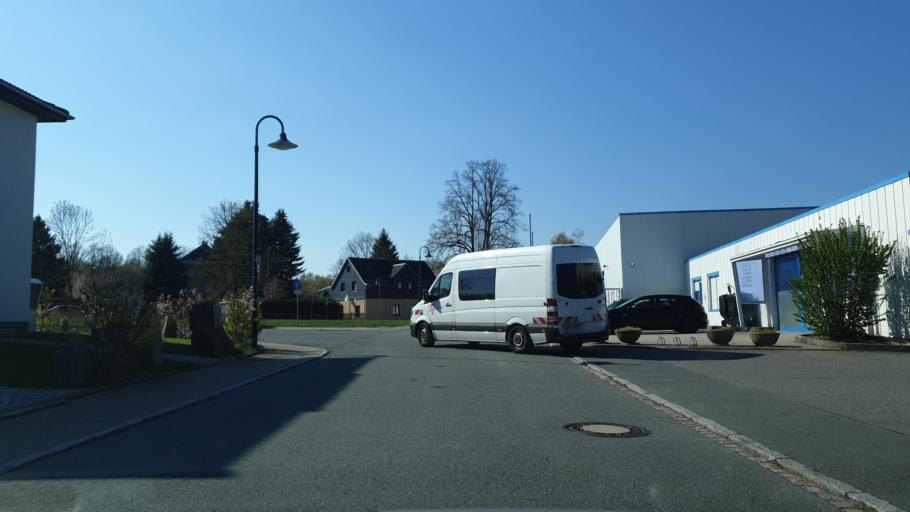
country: DE
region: Saxony
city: Oelsnitz
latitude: 50.7292
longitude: 12.7033
